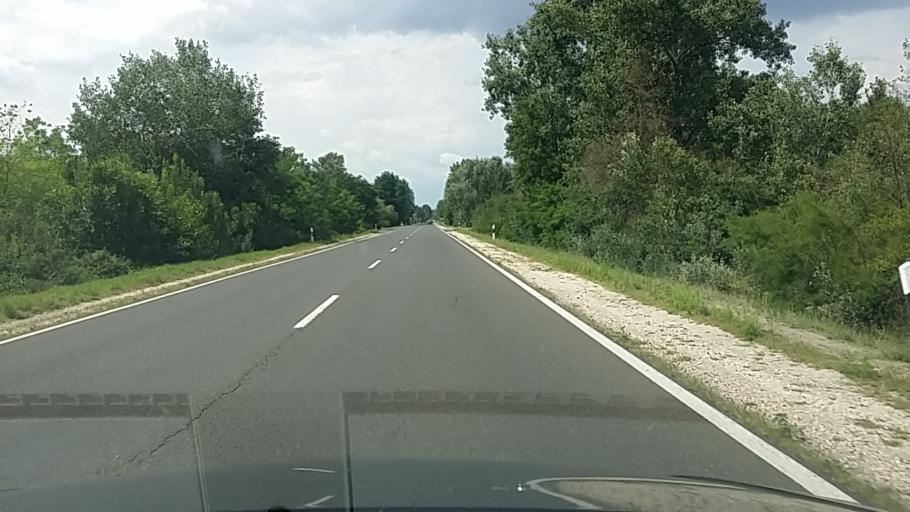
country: HU
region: Pest
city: Taborfalva
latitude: 47.0759
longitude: 19.4924
